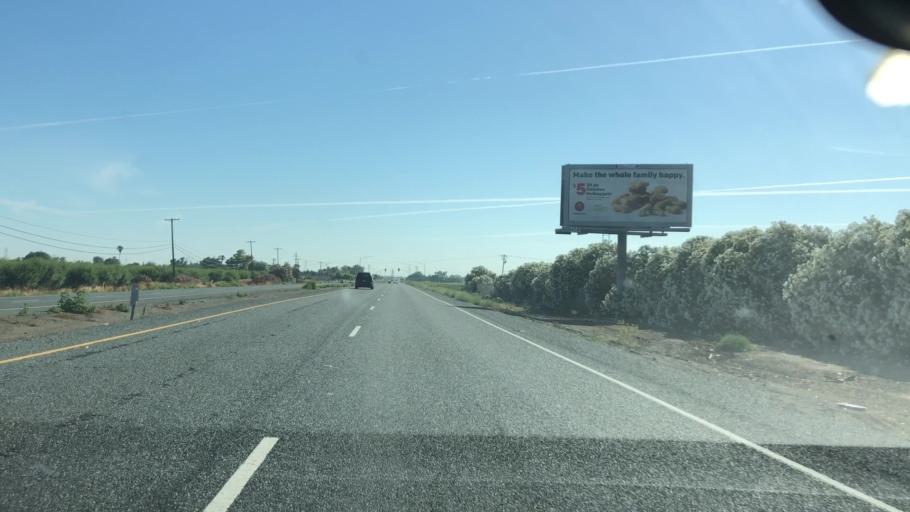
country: US
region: California
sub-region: San Joaquin County
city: Tracy
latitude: 37.7434
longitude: -121.3649
